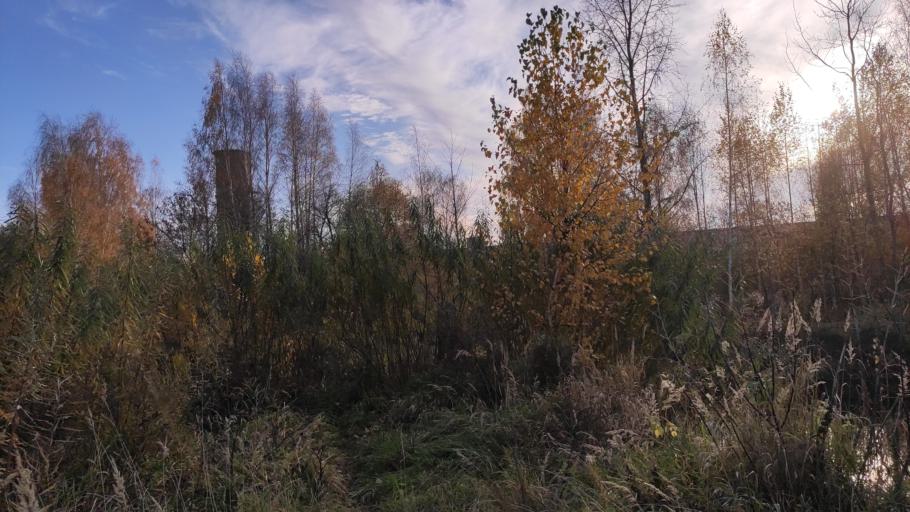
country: RU
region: Moskovskaya
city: Noginsk
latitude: 55.8743
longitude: 38.4589
